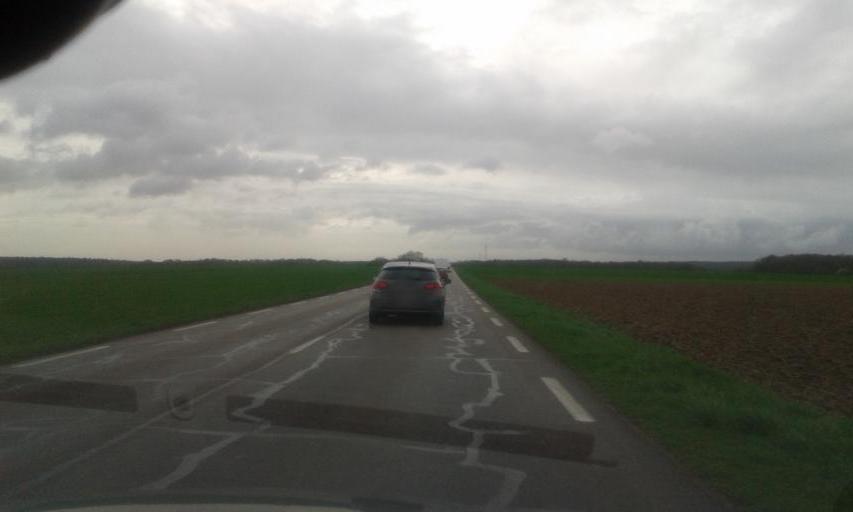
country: FR
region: Haute-Normandie
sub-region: Departement de l'Eure
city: Fleury-sur-Andelle
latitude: 49.3805
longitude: 1.3207
